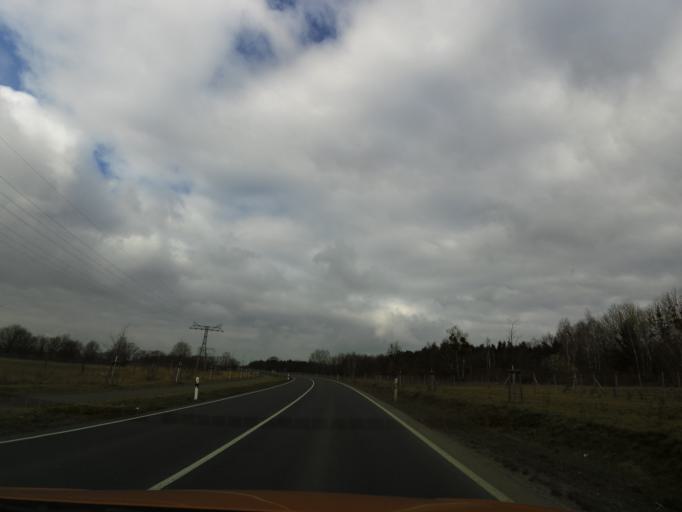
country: DE
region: Brandenburg
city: Wustermark
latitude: 52.4645
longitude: 12.9721
